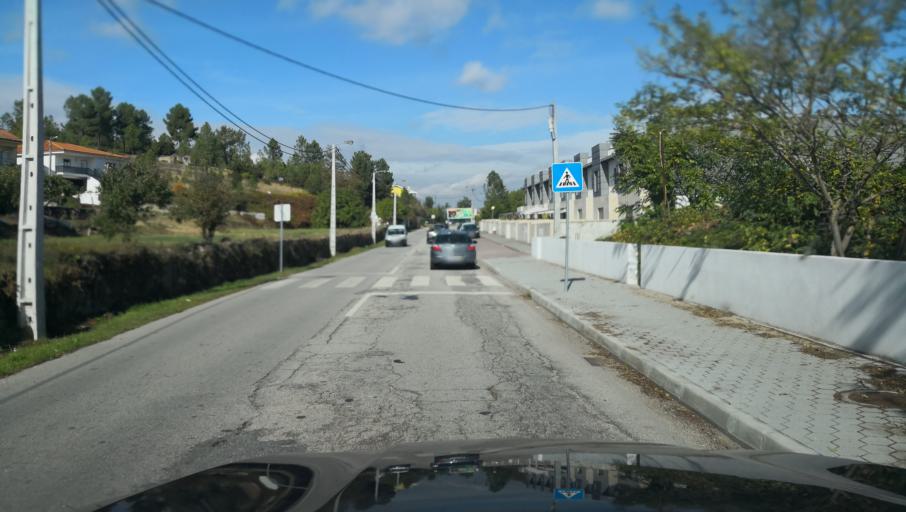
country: PT
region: Vila Real
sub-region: Chaves
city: Chaves
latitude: 41.7336
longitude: -7.4781
